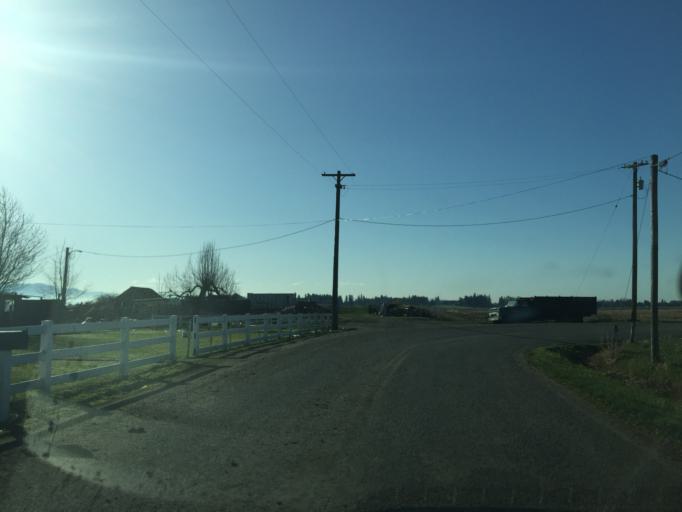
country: US
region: Washington
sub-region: Whatcom County
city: Lynden
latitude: 48.9316
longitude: -122.4525
